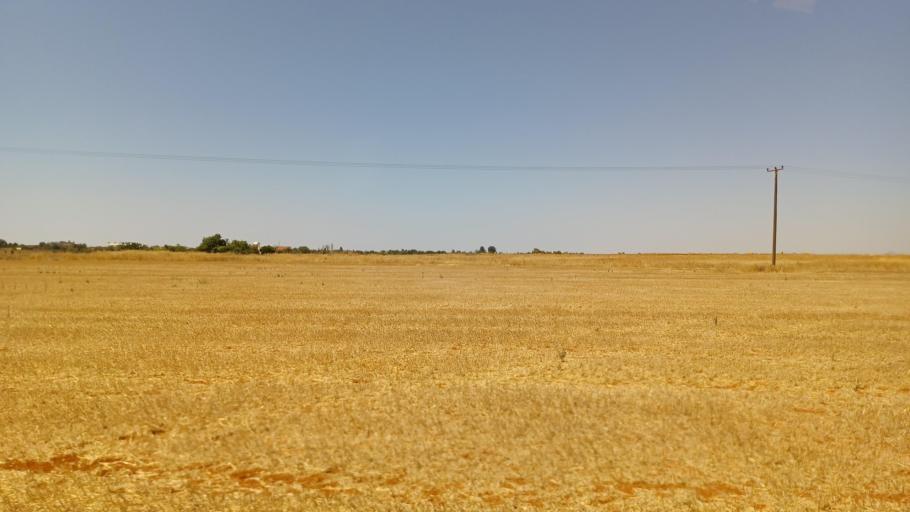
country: CY
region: Larnaka
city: Xylotymbou
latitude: 35.0266
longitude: 33.7253
